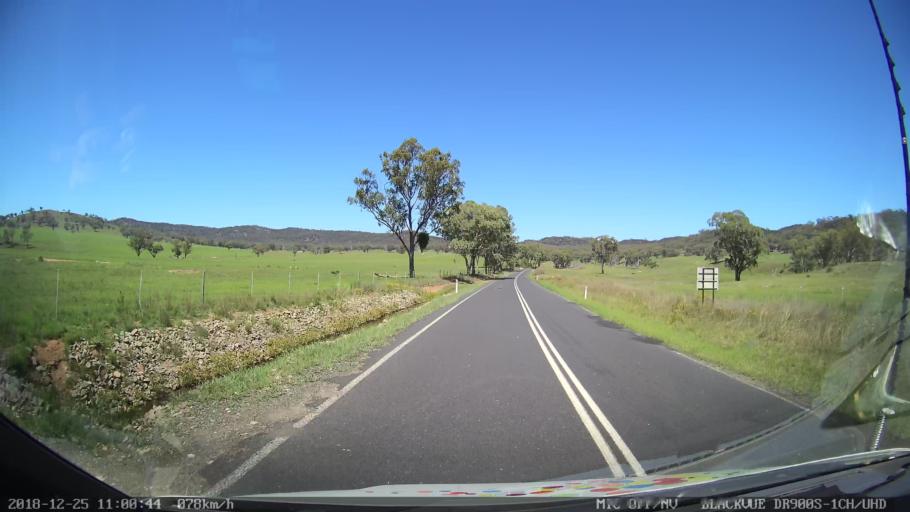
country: AU
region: New South Wales
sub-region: Upper Hunter Shire
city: Merriwa
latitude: -32.4025
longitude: 150.2112
